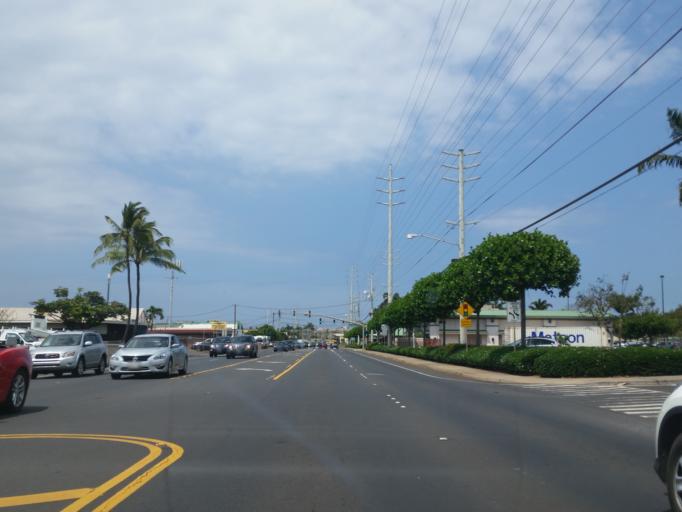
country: US
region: Hawaii
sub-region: Maui County
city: Kahului
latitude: 20.8805
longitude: -156.4564
